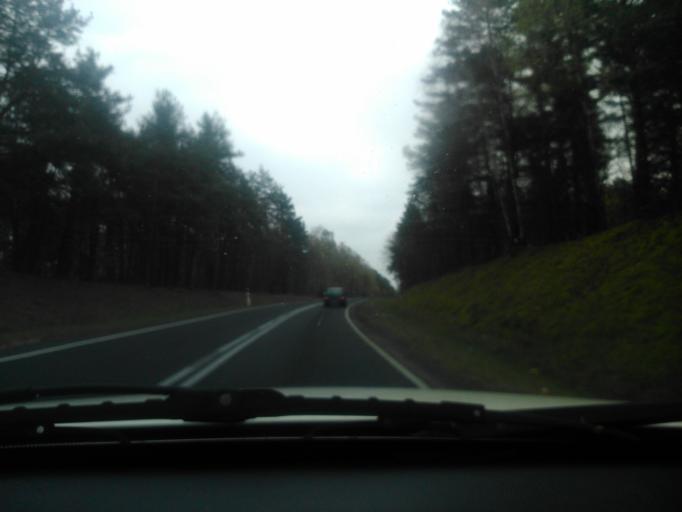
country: PL
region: Warmian-Masurian Voivodeship
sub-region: Powiat dzialdowski
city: Ilowo -Osada
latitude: 53.1175
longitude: 20.2762
